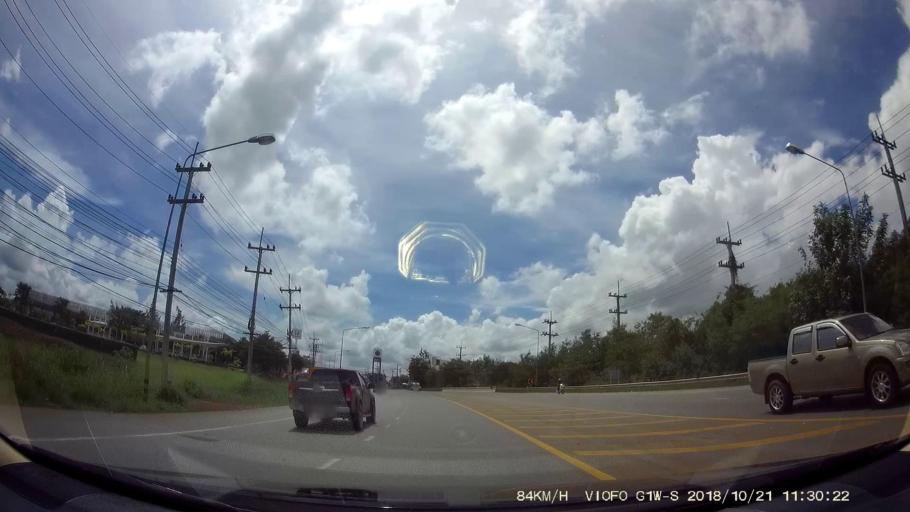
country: TH
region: Chaiyaphum
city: Chaiyaphum
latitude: 15.7792
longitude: 102.0252
